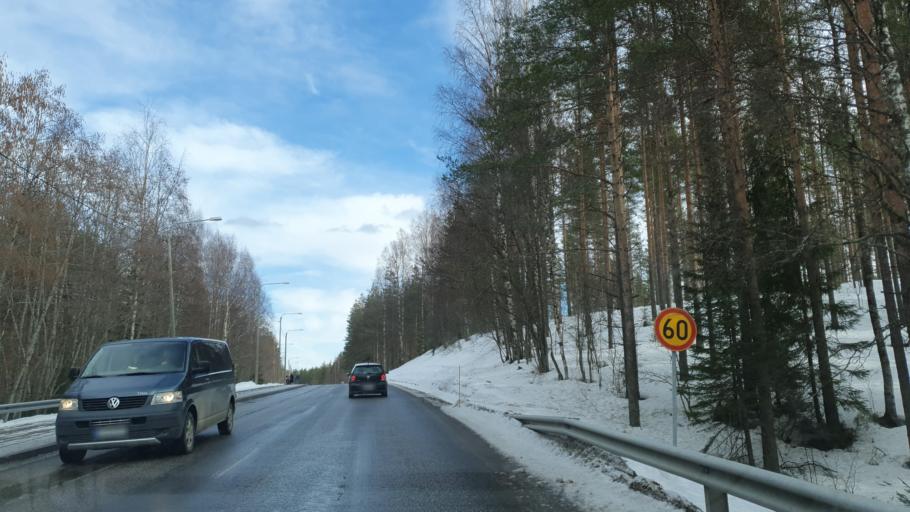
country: FI
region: Kainuu
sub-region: Kajaani
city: Vuokatti
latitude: 64.1456
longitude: 28.2790
